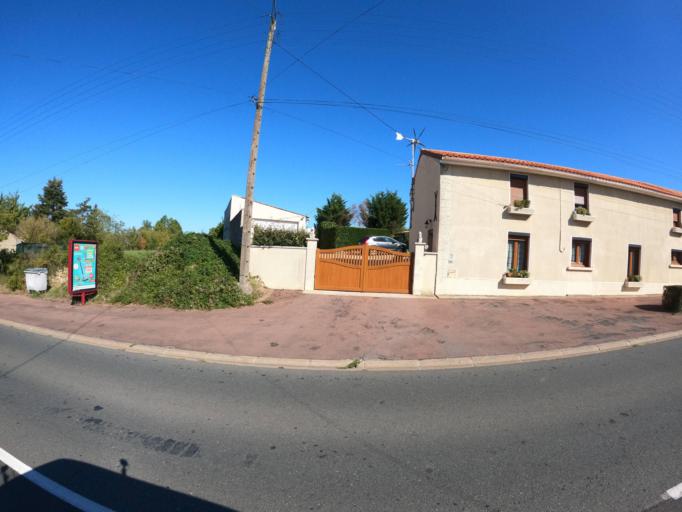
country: FR
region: Poitou-Charentes
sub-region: Departement de la Vienne
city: Ayron
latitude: 46.6597
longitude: 0.0665
